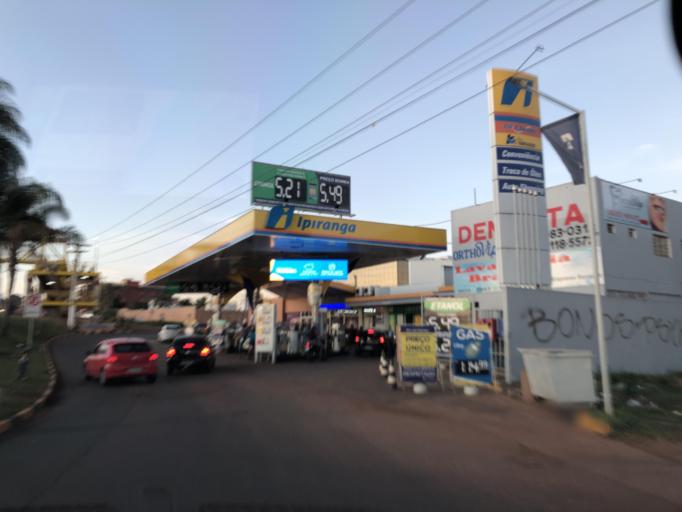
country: BR
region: Goias
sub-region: Luziania
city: Luziania
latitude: -16.0553
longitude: -47.9819
